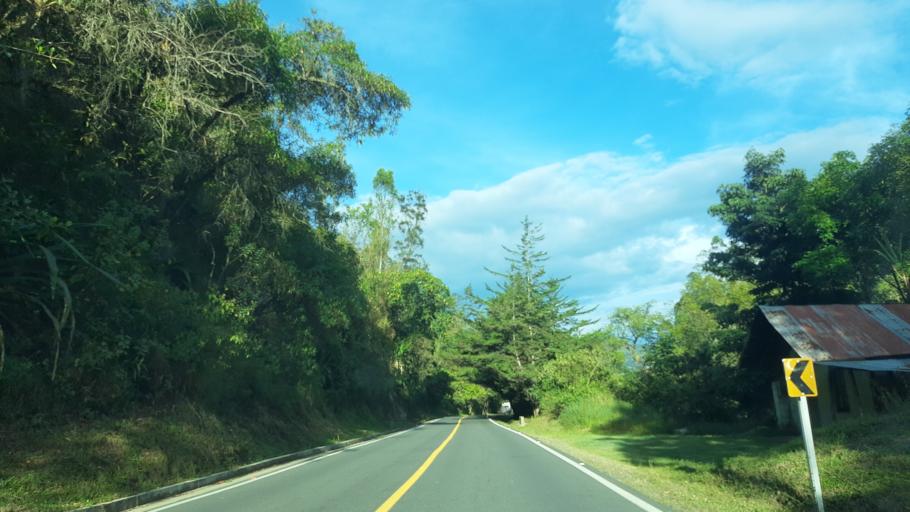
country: CO
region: Cundinamarca
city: Macheta
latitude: 5.0755
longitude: -73.5688
